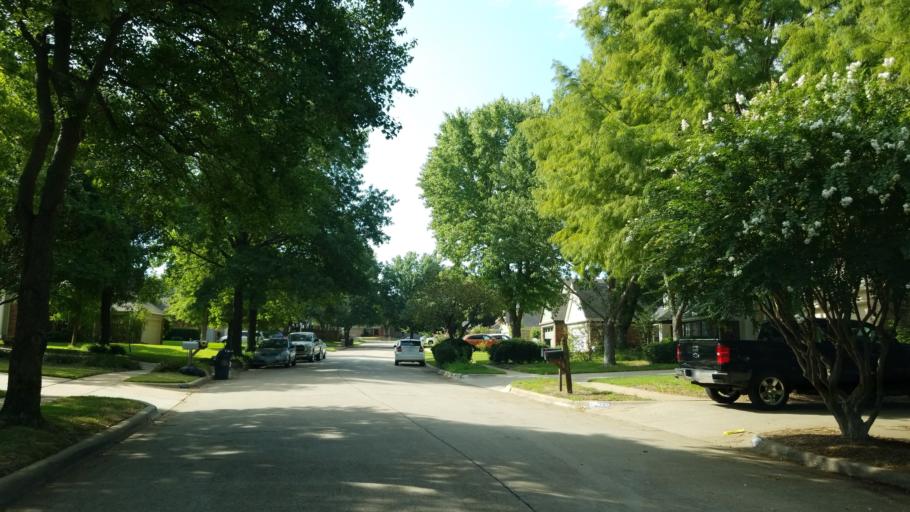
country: US
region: Texas
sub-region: Tarrant County
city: Grapevine
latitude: 32.8919
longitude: -97.0861
